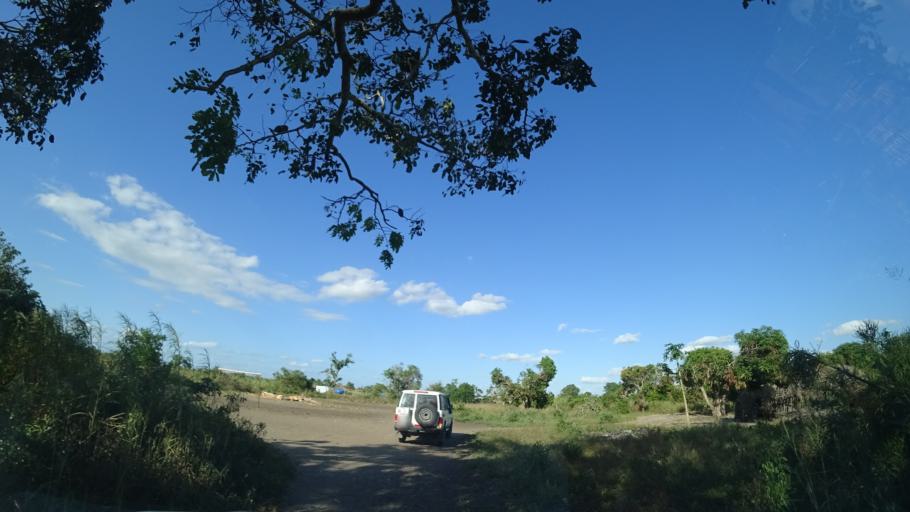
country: MZ
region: Sofala
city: Dondo
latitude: -19.3544
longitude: 34.5883
